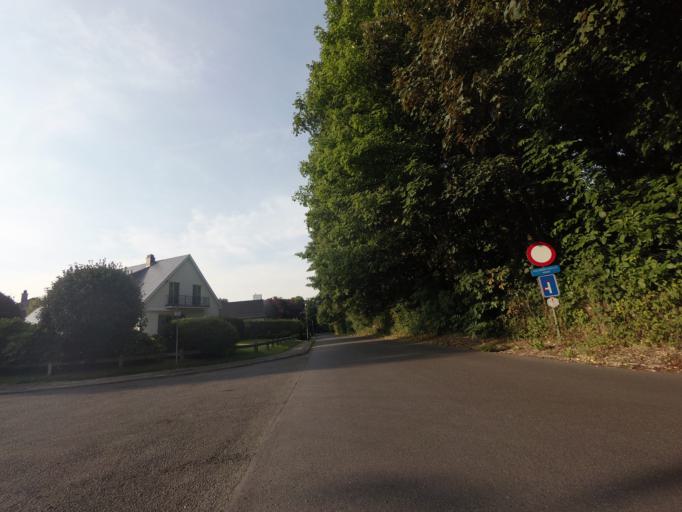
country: BE
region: Flanders
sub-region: Provincie Vlaams-Brabant
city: Vilvoorde
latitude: 50.9313
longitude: 4.4021
